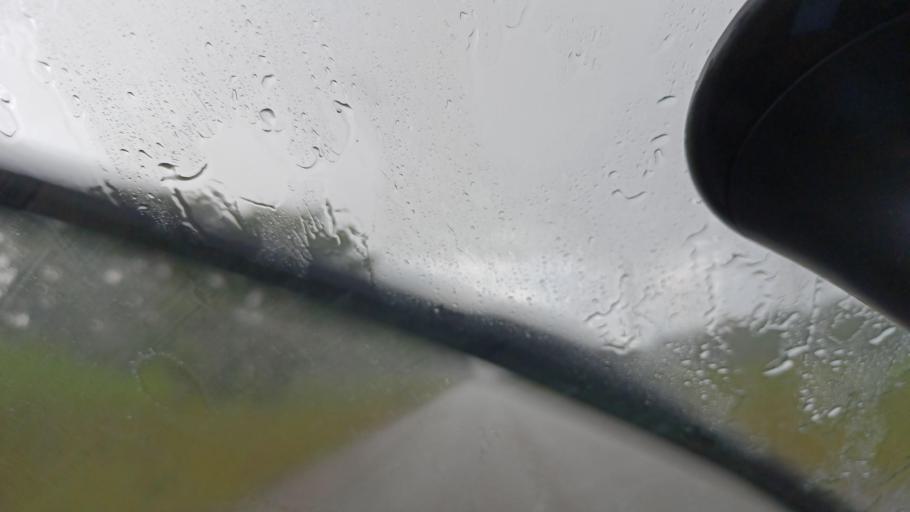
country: ZM
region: North-Western
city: Kasempa
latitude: -13.0935
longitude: 25.9199
